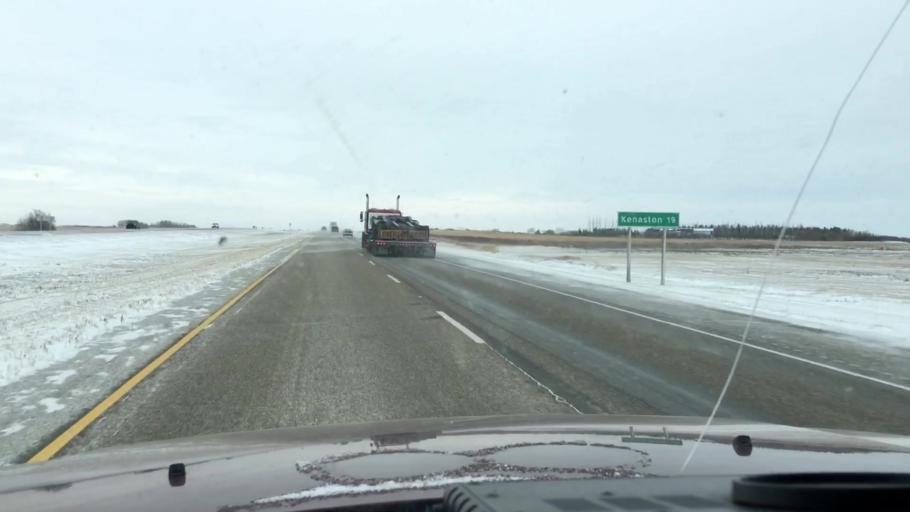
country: CA
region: Saskatchewan
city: Saskatoon
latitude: 51.6321
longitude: -106.4276
